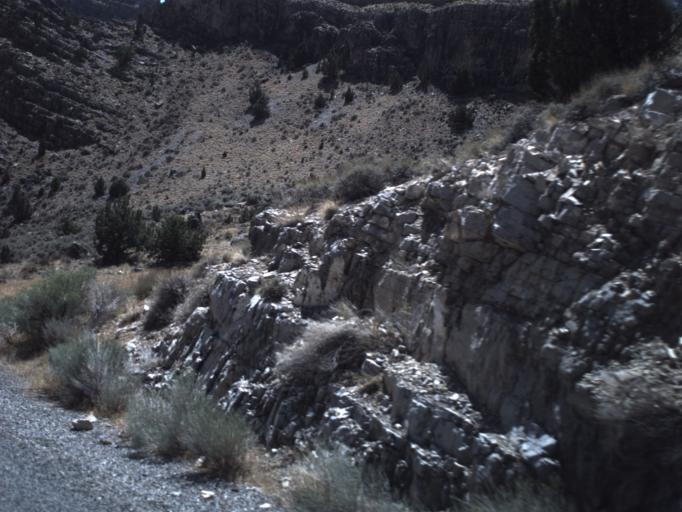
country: US
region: Utah
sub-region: Beaver County
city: Milford
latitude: 39.0849
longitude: -113.5763
